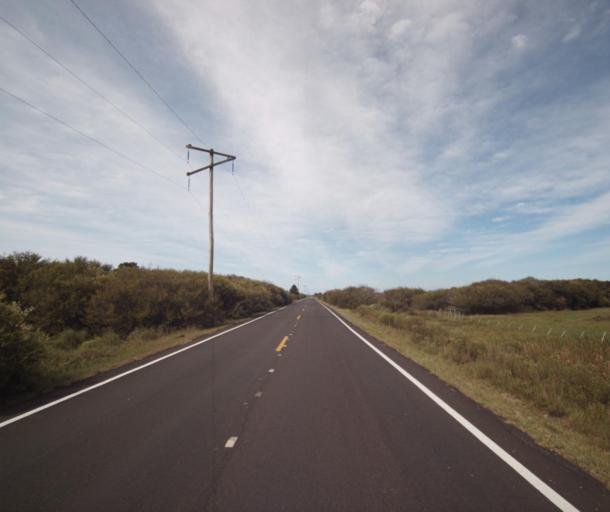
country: BR
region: Rio Grande do Sul
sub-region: Rio Grande
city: Rio Grande
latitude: -31.9149
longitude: -51.9403
